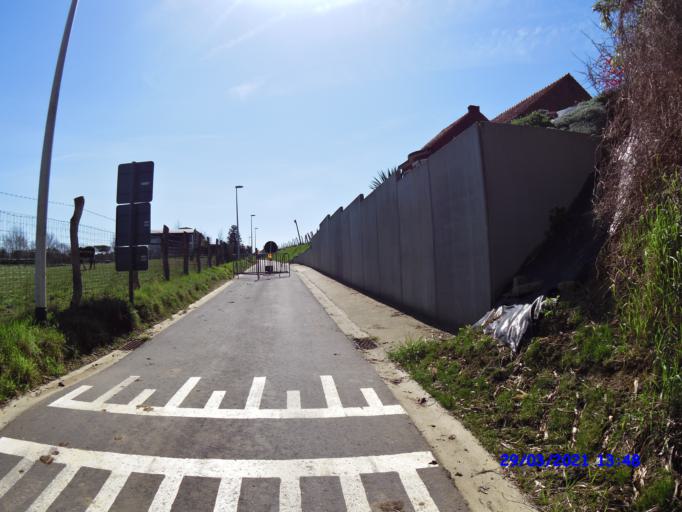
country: BE
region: Flanders
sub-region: Provincie Vlaams-Brabant
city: Diest
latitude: 50.9837
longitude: 5.0222
